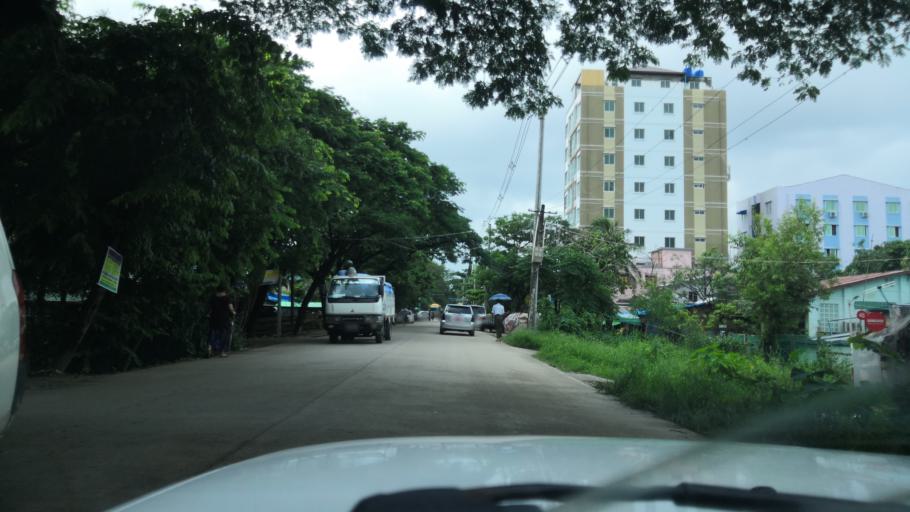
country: MM
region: Yangon
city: Yangon
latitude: 16.8765
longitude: 96.1821
